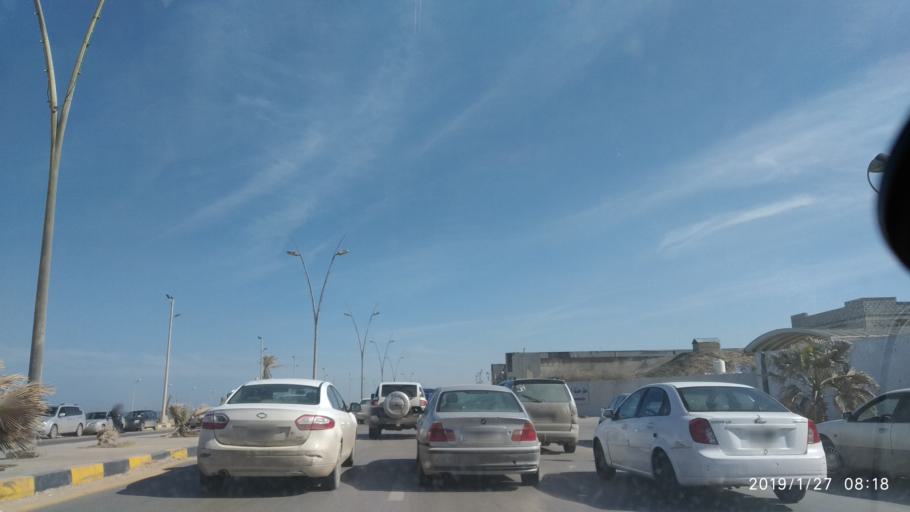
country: LY
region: Tripoli
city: Tagiura
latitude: 32.9079
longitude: 13.2725
